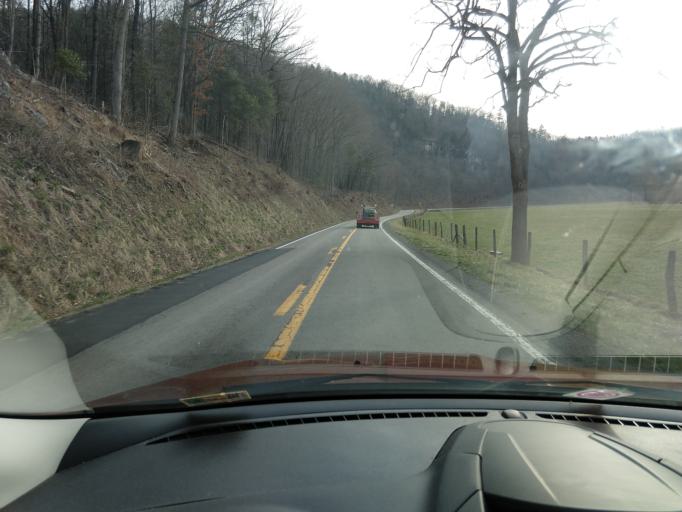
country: US
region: West Virginia
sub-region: Pendleton County
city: Franklin
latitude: 38.6037
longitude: -79.3767
